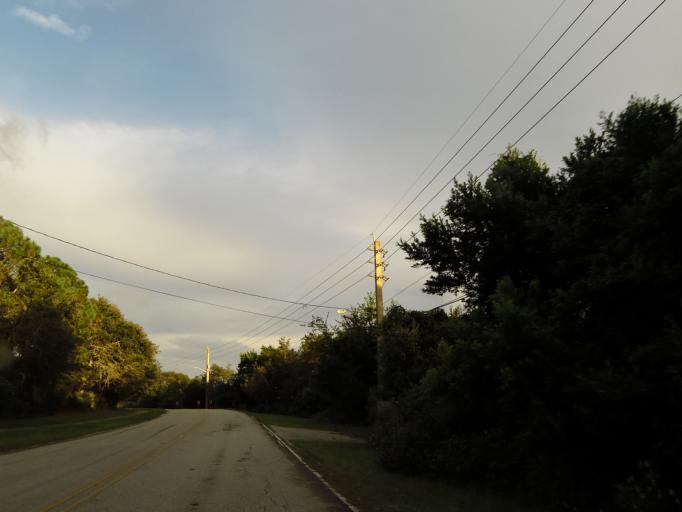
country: US
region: Florida
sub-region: Duval County
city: Atlantic Beach
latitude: 30.3788
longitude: -81.4949
